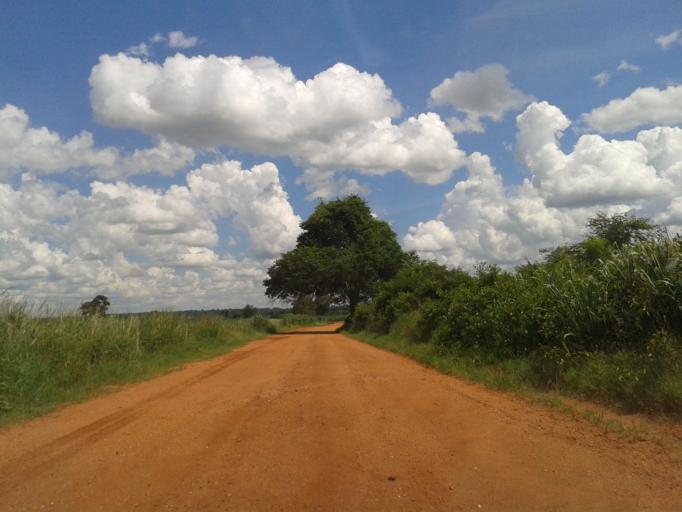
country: BR
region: Minas Gerais
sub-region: Santa Vitoria
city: Santa Vitoria
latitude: -19.1622
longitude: -50.5973
